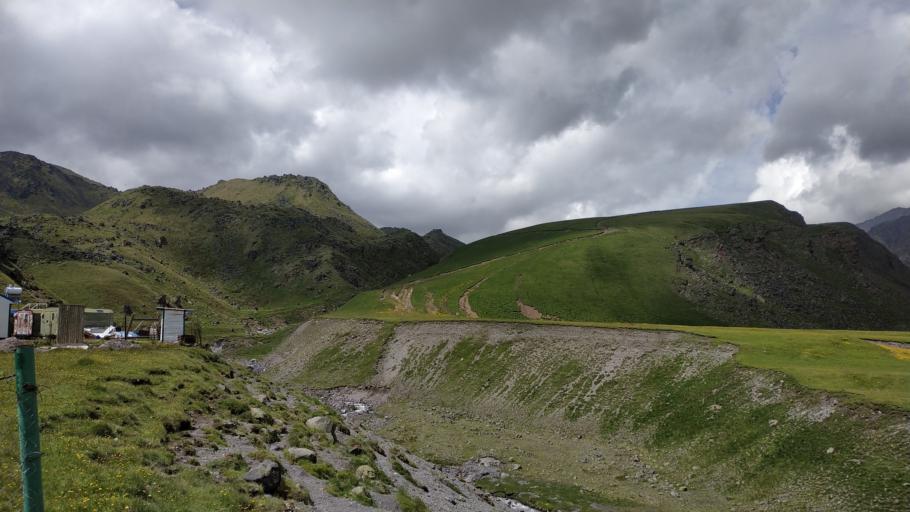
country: RU
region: Kabardino-Balkariya
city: Terskol
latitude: 43.4302
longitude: 42.5113
